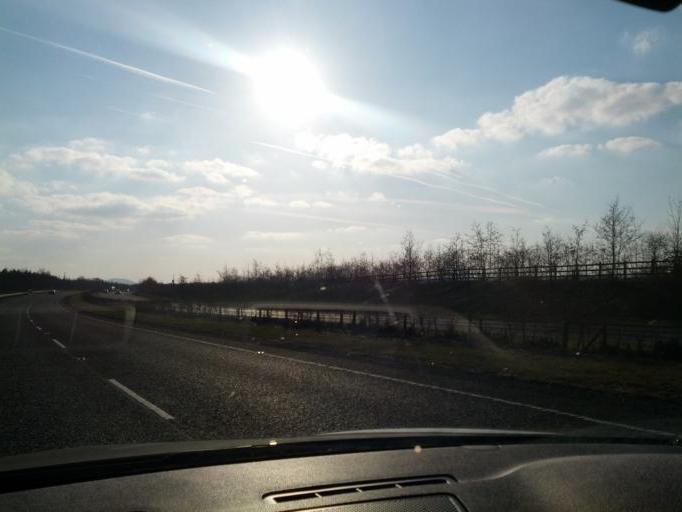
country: IE
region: Leinster
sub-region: Kildare
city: Monasterevin
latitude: 53.1182
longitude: -7.0449
